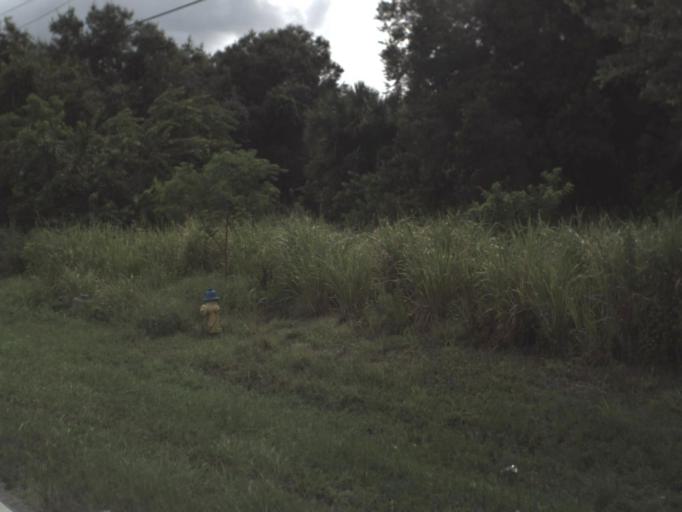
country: US
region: Florida
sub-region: Manatee County
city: Samoset
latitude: 27.4601
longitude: -82.5467
